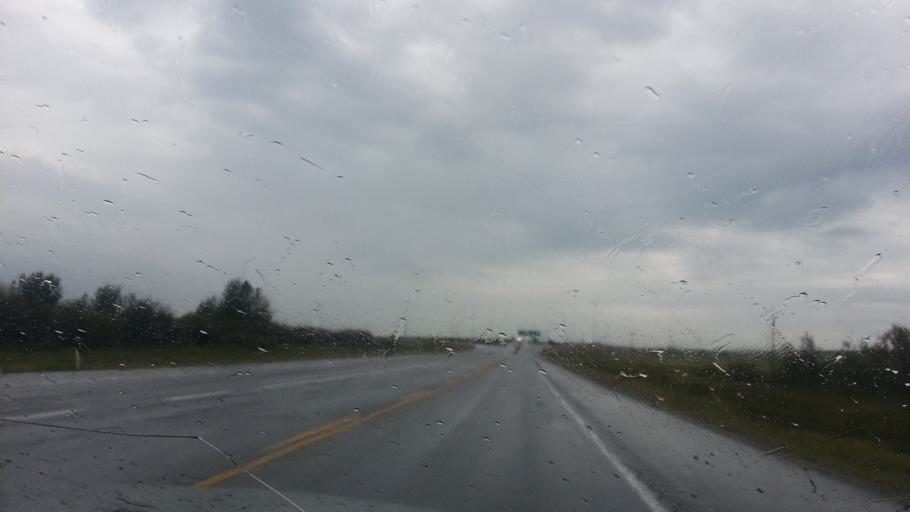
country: CA
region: Alberta
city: Cochrane
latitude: 51.0795
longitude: -114.4669
